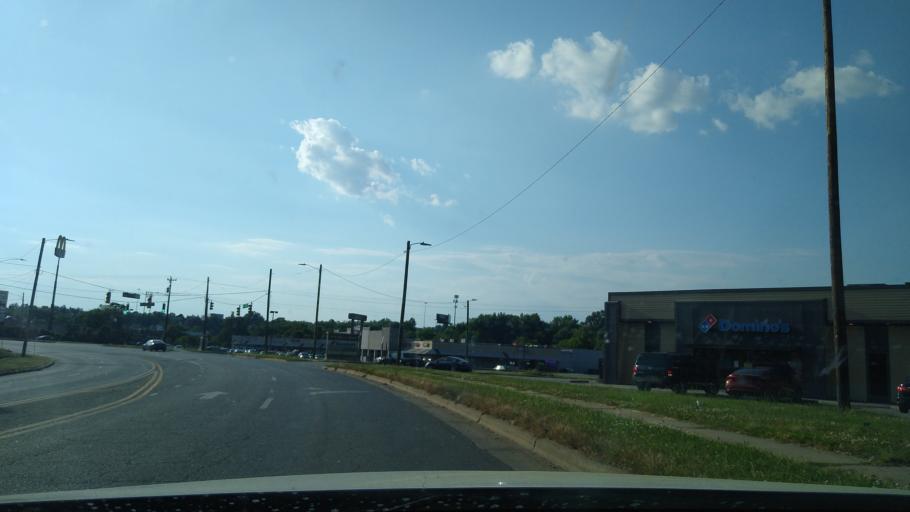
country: US
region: North Carolina
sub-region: Guilford County
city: Greensboro
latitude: 36.0409
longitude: -79.7697
